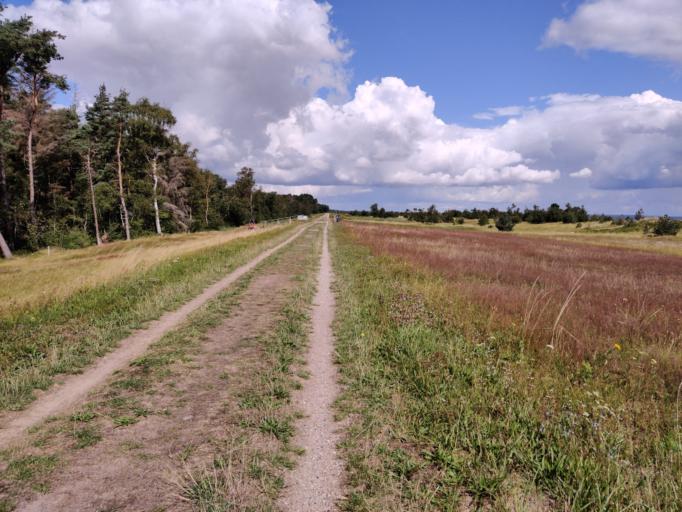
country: DK
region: Zealand
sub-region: Guldborgsund Kommune
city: Nykobing Falster
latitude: 54.6337
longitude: 11.9614
